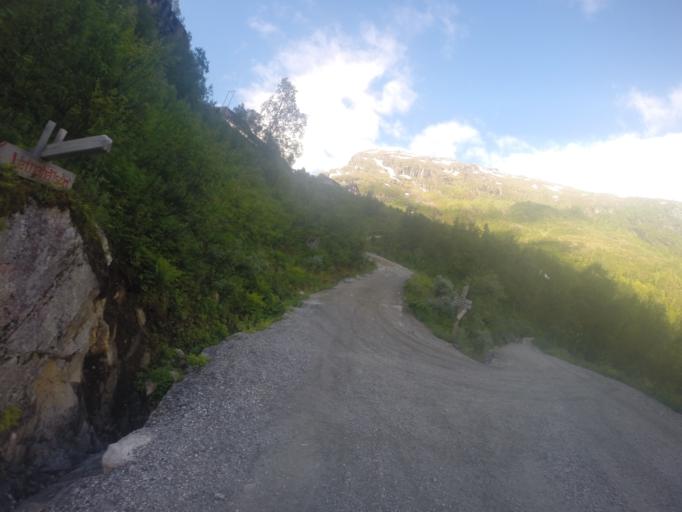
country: NO
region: Sogn og Fjordane
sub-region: Aurland
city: Aurlandsvangen
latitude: 60.7407
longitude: 7.1256
